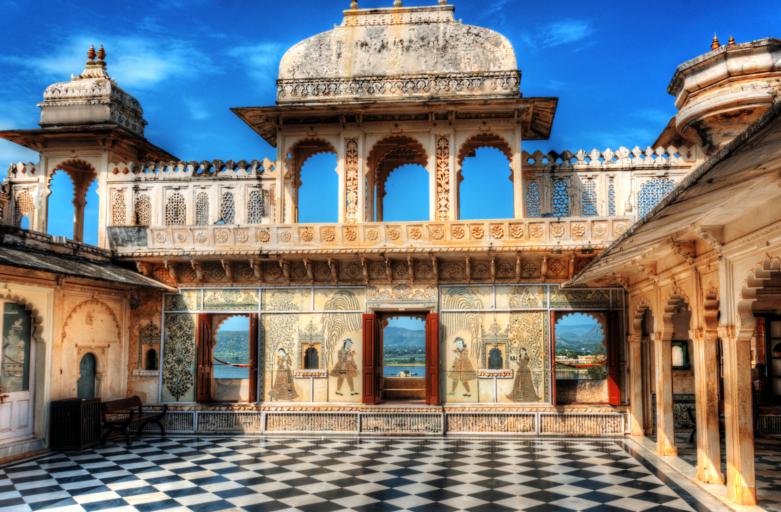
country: IN
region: Rajasthan
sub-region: Udaipur
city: Udaipur
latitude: 24.5788
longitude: 73.6847
